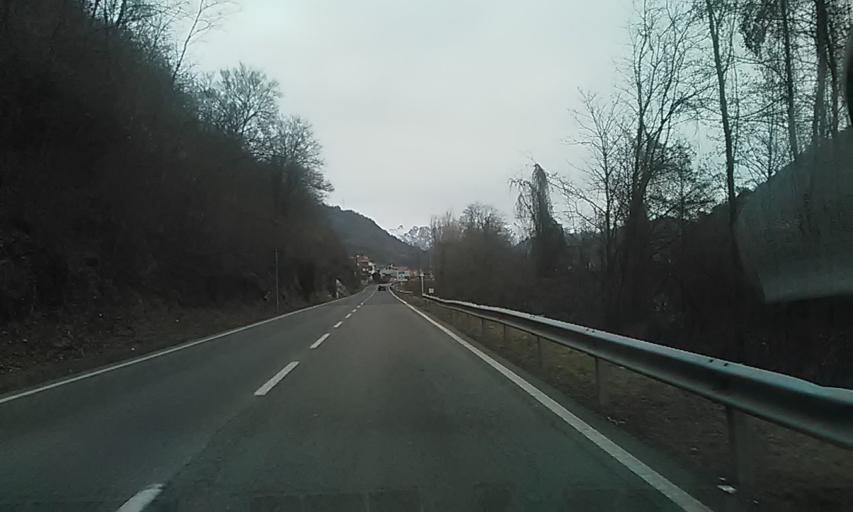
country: IT
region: Piedmont
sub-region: Provincia di Vercelli
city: Borgosesia
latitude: 45.7344
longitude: 8.2597
